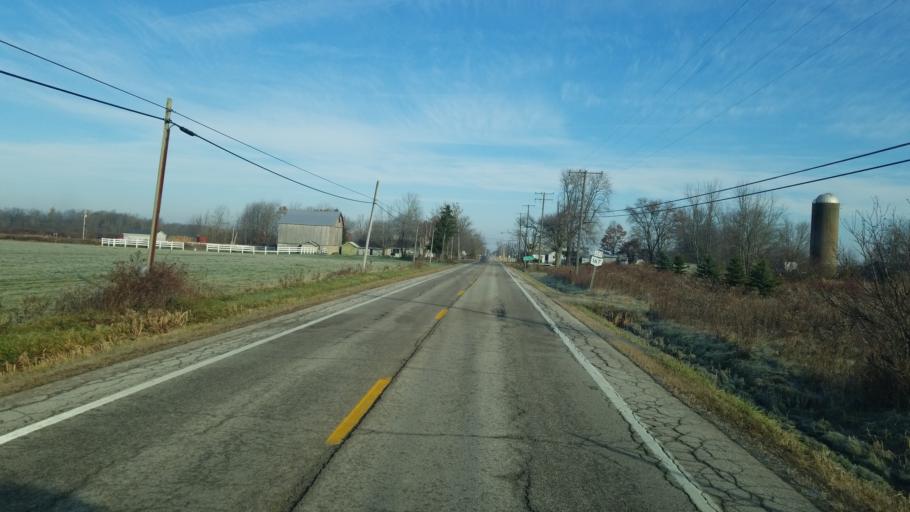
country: US
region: Ohio
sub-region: Ashtabula County
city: Jefferson
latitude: 41.7490
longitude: -80.6676
